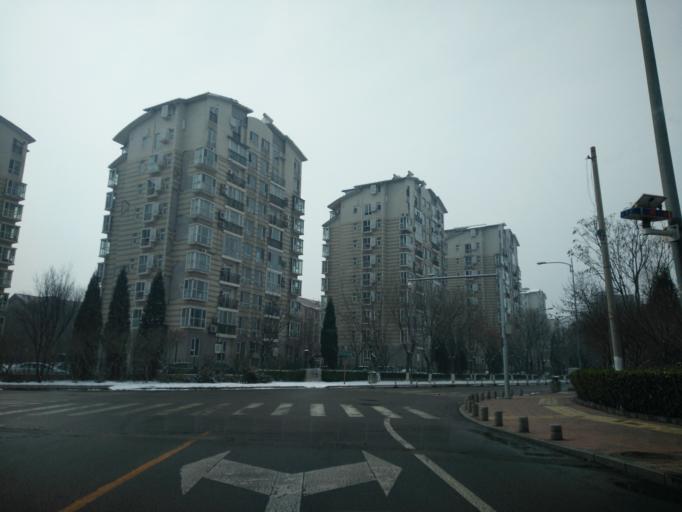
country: CN
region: Beijing
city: Jiugong
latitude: 39.7931
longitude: 116.4976
